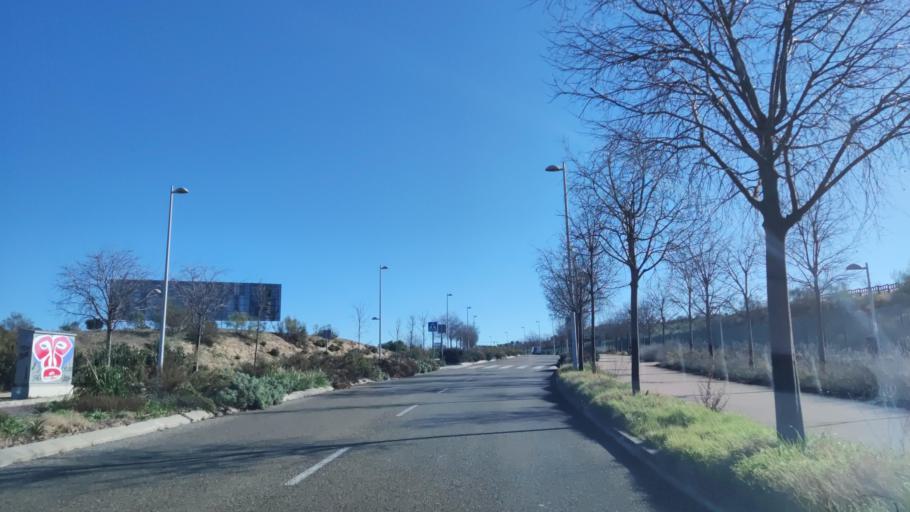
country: ES
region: Madrid
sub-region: Provincia de Madrid
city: Hortaleza
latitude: 40.4979
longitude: -3.6346
